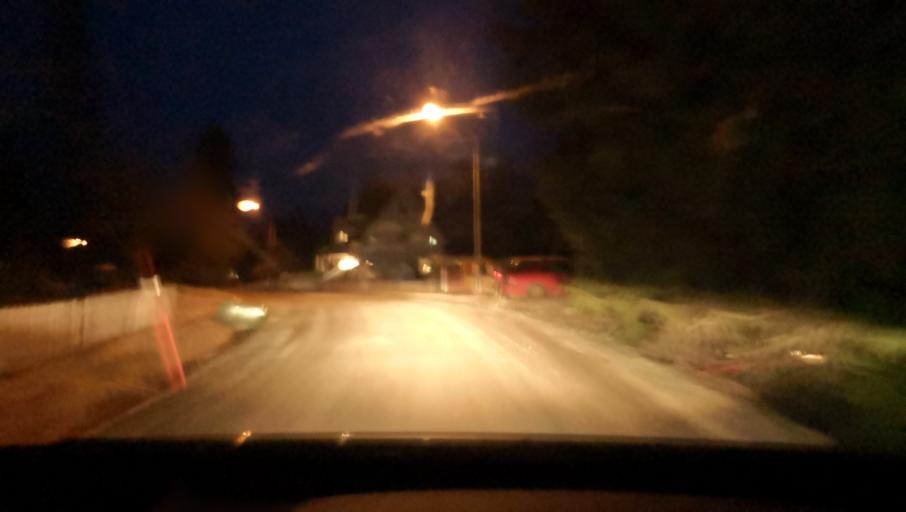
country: SE
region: Vaestmanland
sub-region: Skinnskattebergs Kommun
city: Skinnskatteberg
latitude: 59.6651
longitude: 15.5277
